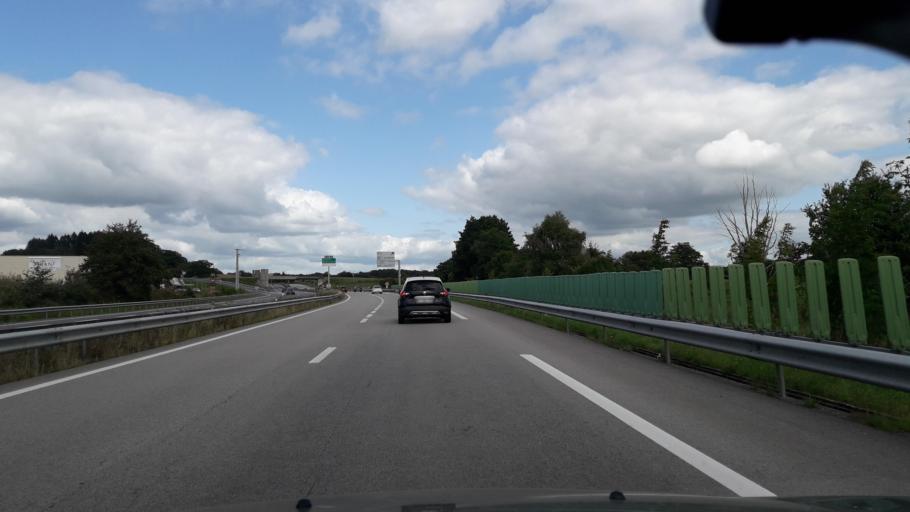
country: FR
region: Limousin
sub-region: Departement de la Creuse
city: La Souterraine
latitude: 46.2277
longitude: 1.5042
